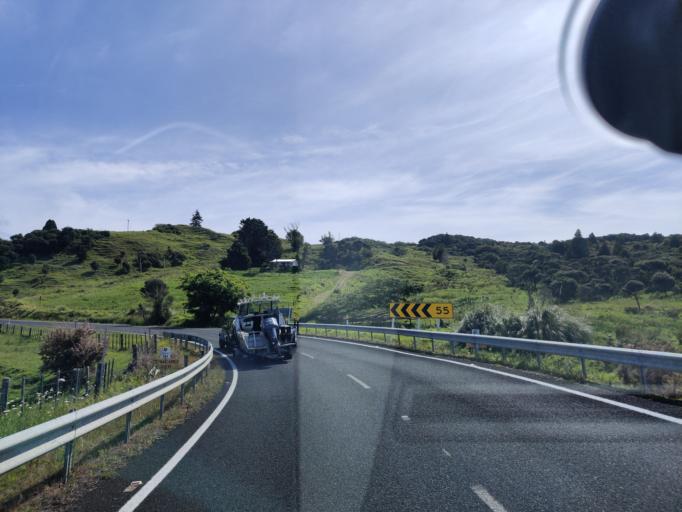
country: NZ
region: Northland
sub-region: Far North District
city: Kaitaia
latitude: -35.4747
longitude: 173.4595
